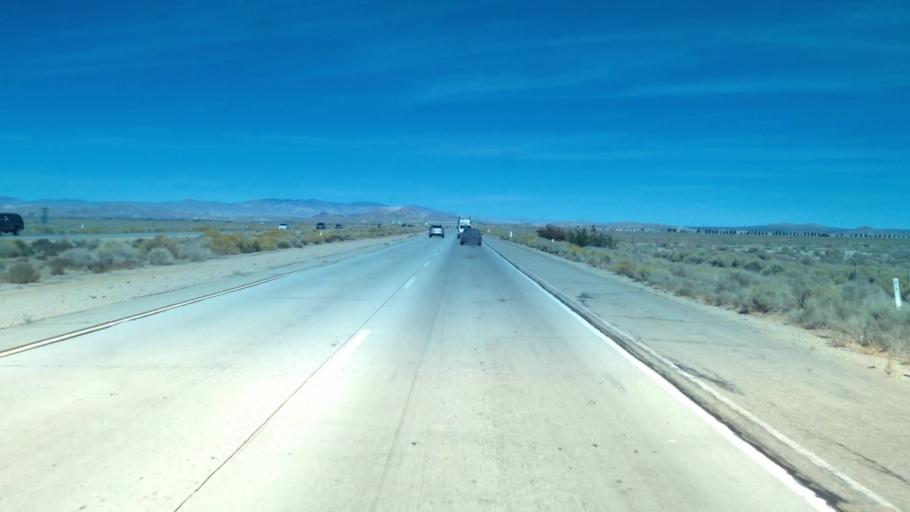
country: US
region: California
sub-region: Los Angeles County
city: Lancaster
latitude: 34.7626
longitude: -118.1704
